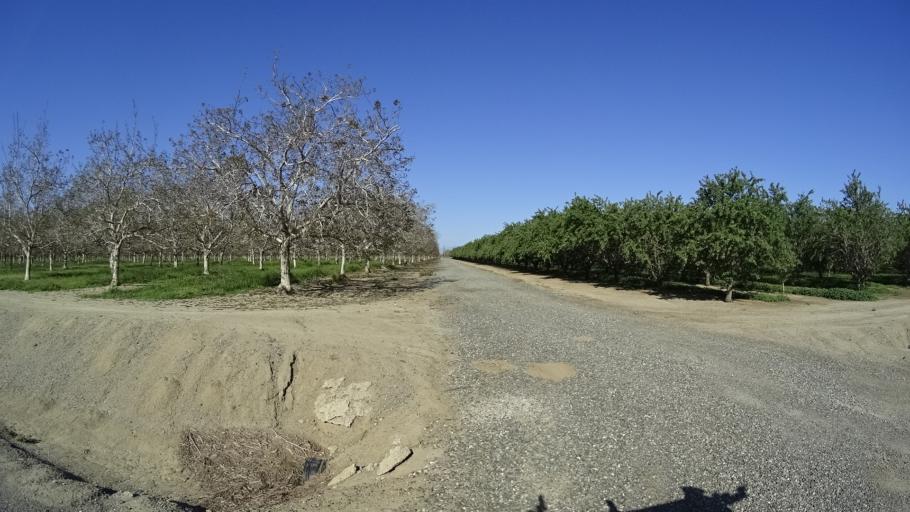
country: US
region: California
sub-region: Glenn County
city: Hamilton City
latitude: 39.7044
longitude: -122.0642
